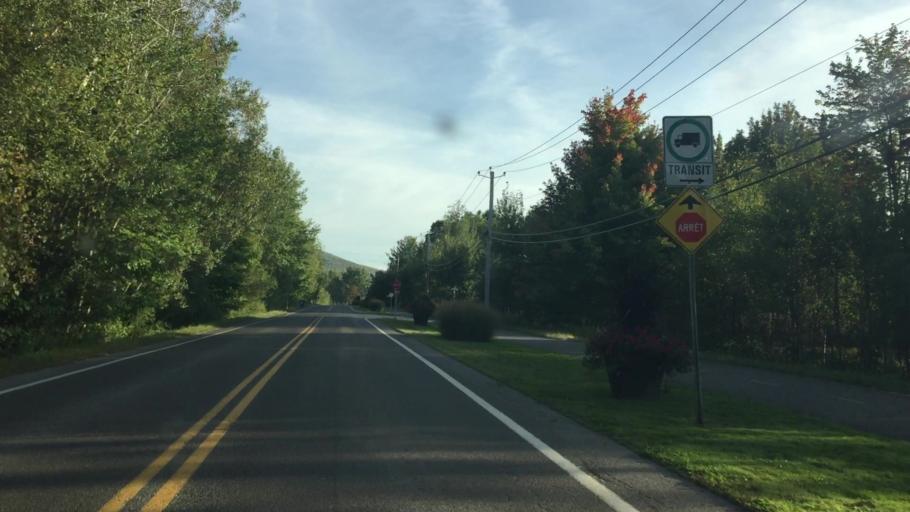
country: CA
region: Quebec
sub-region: Monteregie
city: Bromont
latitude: 45.3130
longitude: -72.6572
